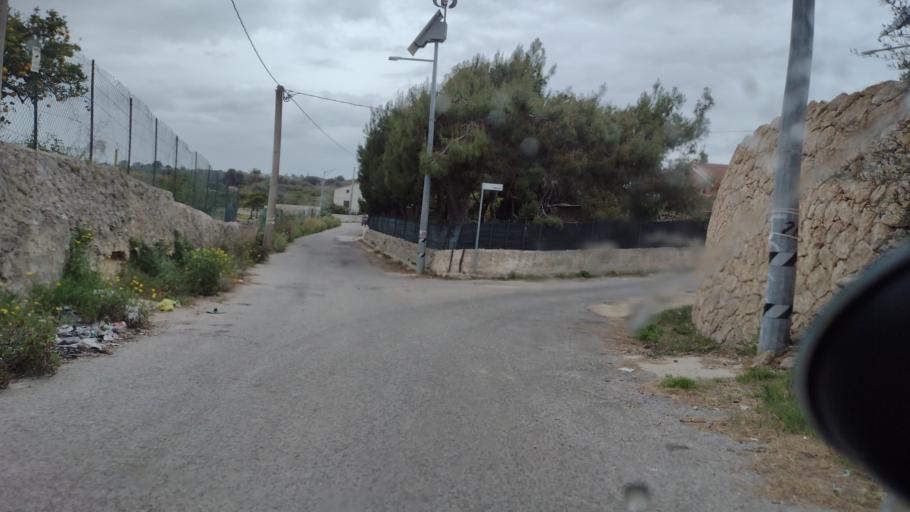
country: IT
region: Sicily
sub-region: Provincia di Siracusa
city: Avola
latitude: 36.8841
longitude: 15.1261
